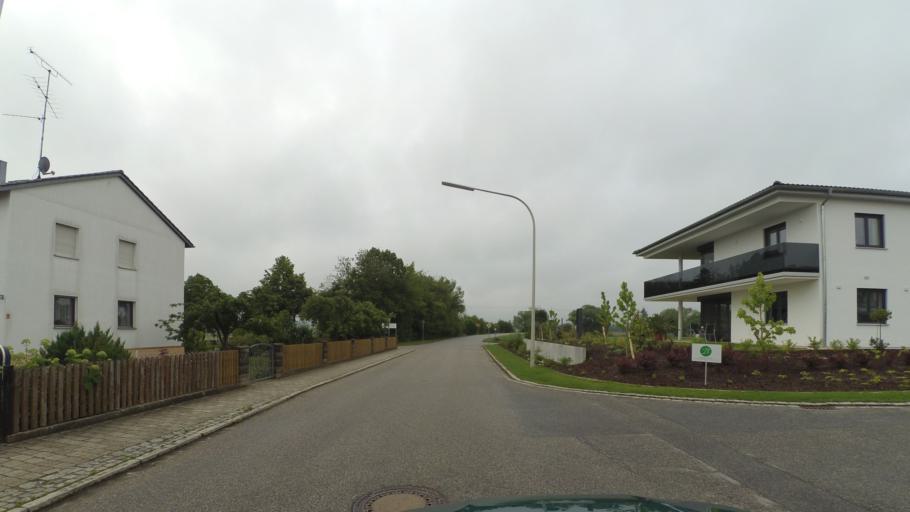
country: DE
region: Bavaria
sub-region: Lower Bavaria
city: Laberweinting
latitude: 48.7889
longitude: 12.2839
